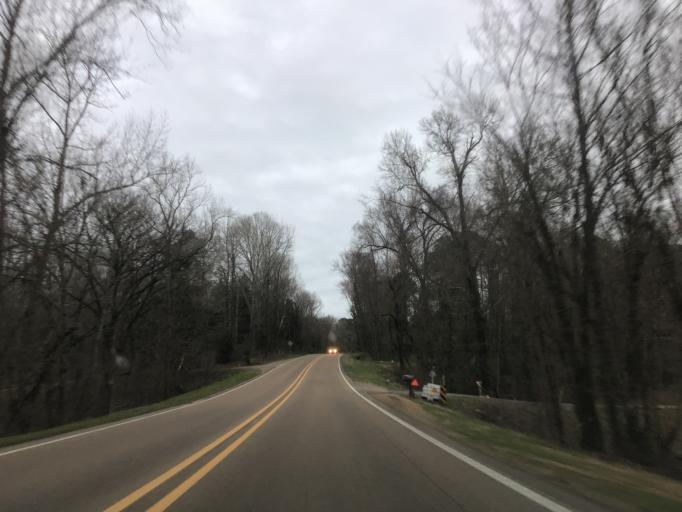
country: US
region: Mississippi
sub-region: Warren County
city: Beechwood
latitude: 32.2818
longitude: -90.7826
